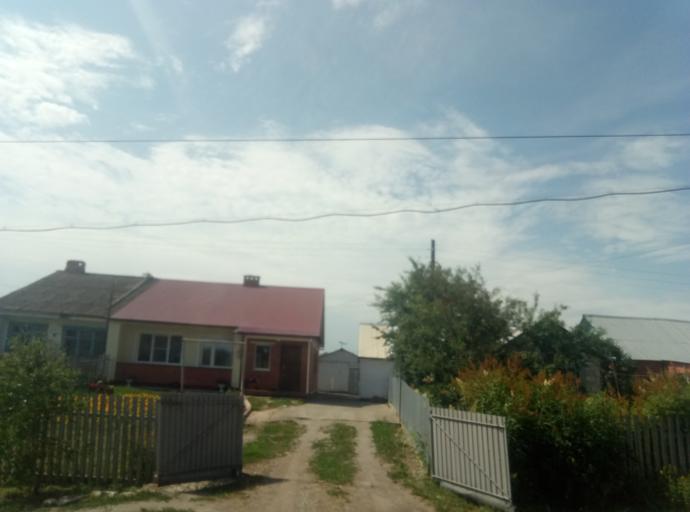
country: RU
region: Tula
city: Dubovka
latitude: 53.9020
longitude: 38.0332
